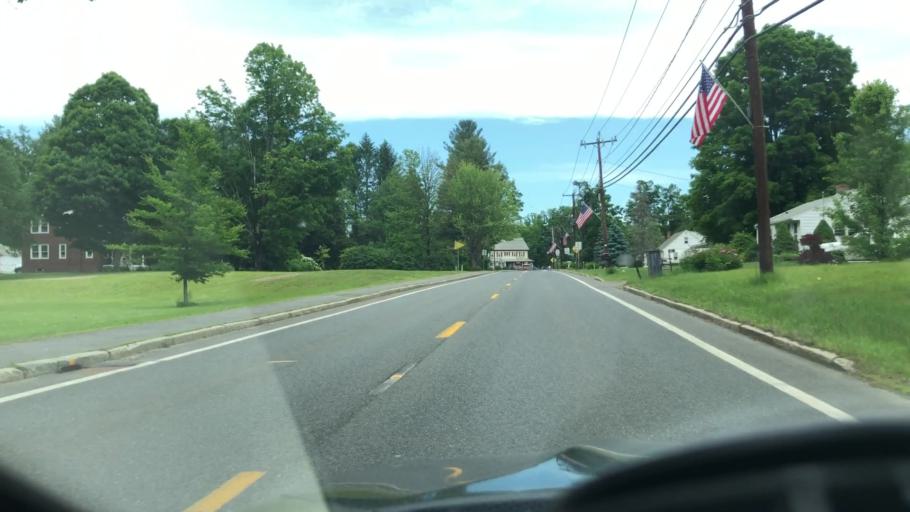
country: US
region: Massachusetts
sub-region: Hampshire County
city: Westhampton
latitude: 42.2460
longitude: -72.8693
